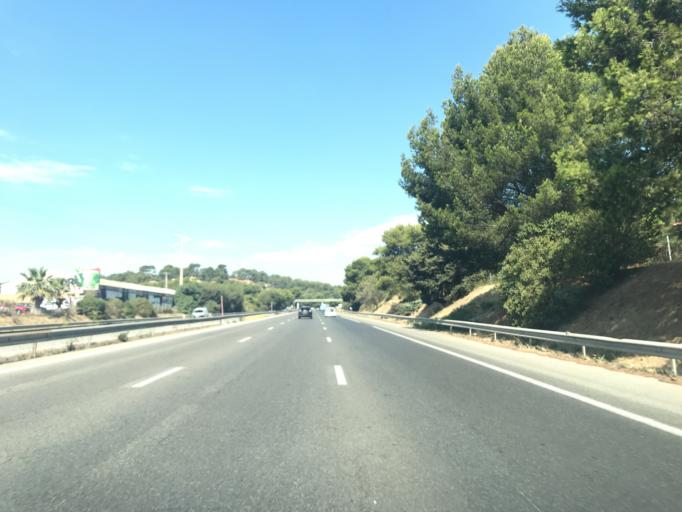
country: FR
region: Provence-Alpes-Cote d'Azur
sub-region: Departement du Var
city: Sanary-sur-Mer
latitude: 43.1274
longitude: 5.8222
